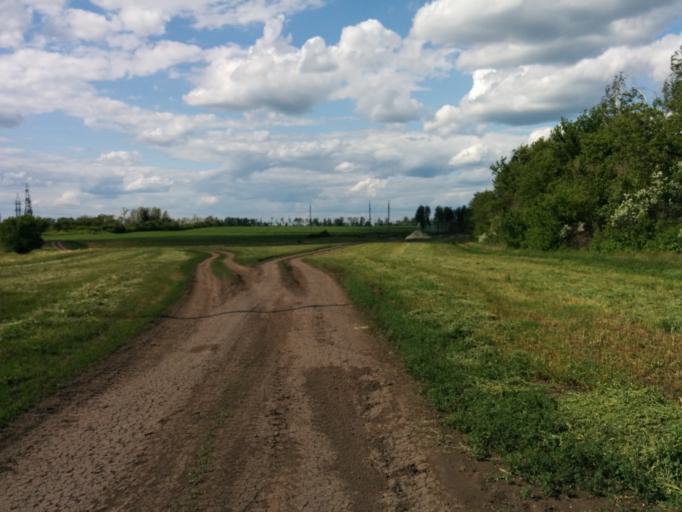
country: RU
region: Tambov
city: Tambov
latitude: 52.7937
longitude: 41.3829
